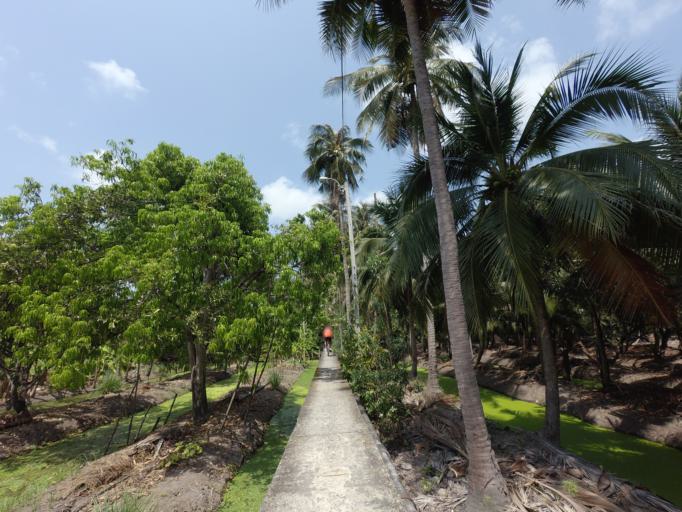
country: TH
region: Bangkok
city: Chom Thong
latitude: 13.6546
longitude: 100.4871
